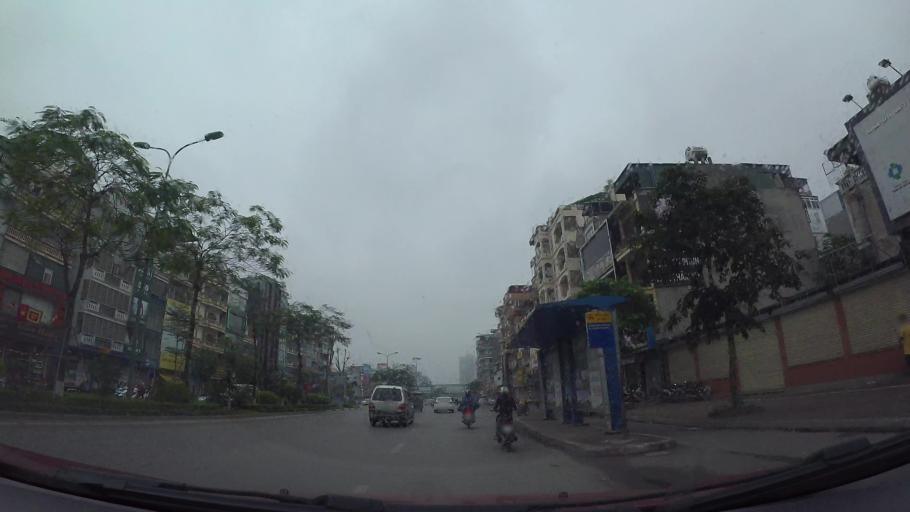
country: VN
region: Ha Noi
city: Dong Da
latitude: 21.0124
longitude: 105.8359
